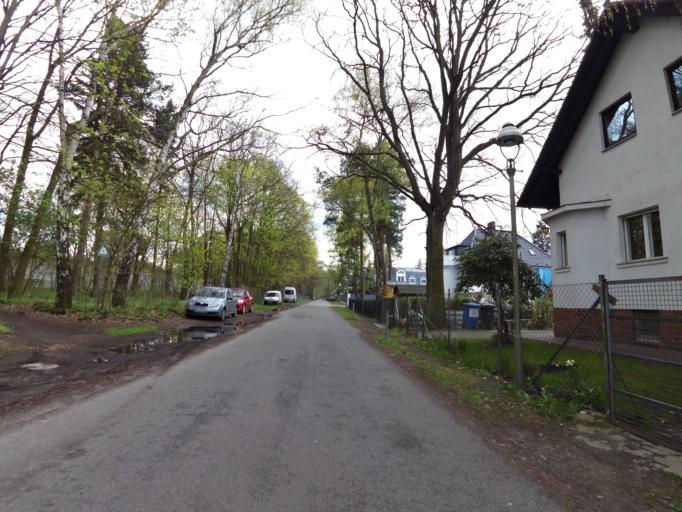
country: DE
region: Berlin
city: Lichtenrade
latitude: 52.3809
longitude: 13.4103
